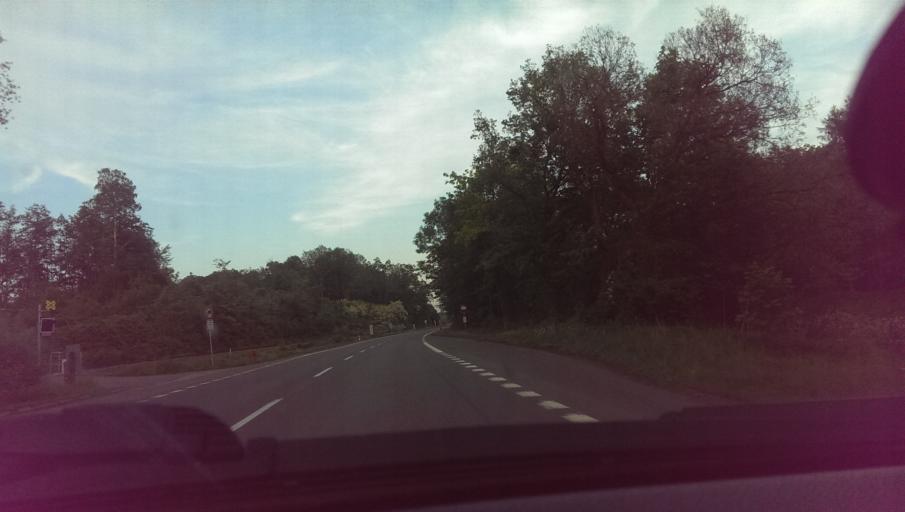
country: CZ
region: Zlin
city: Zasova
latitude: 49.4732
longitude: 18.0174
